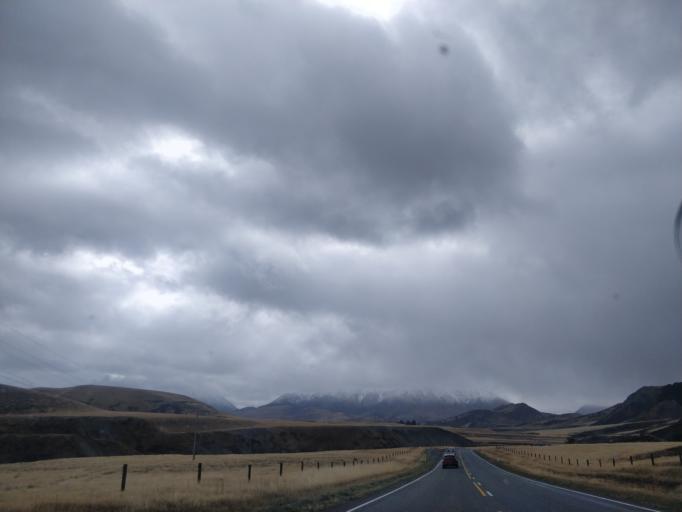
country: NZ
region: Canterbury
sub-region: Ashburton District
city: Methven
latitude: -43.2528
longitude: 171.7147
